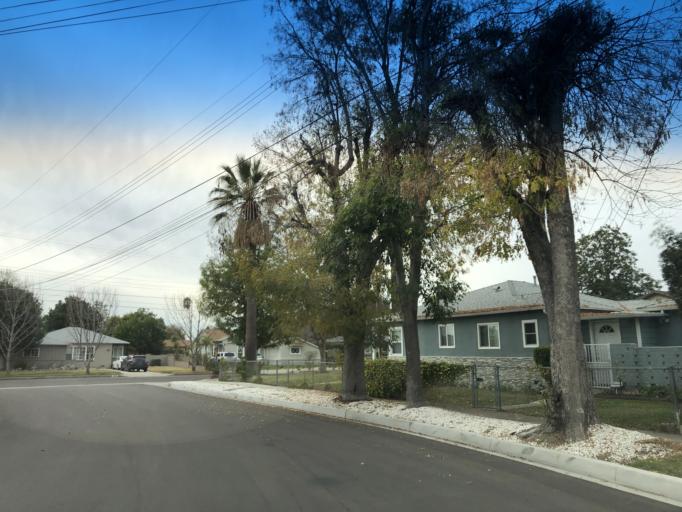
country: US
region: California
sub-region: Los Angeles County
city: Monrovia
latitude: 34.1358
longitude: -118.0148
